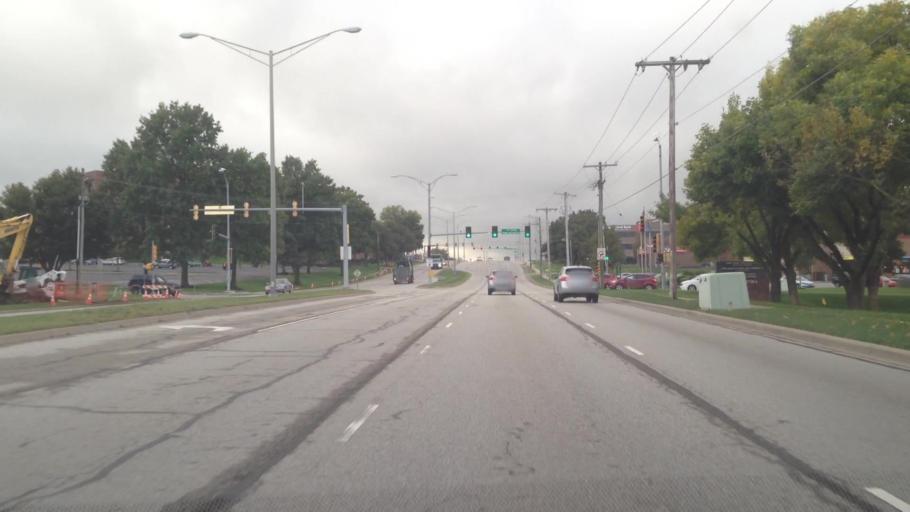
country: US
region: Kansas
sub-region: Johnson County
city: Lenexa
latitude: 38.9309
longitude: -94.7237
